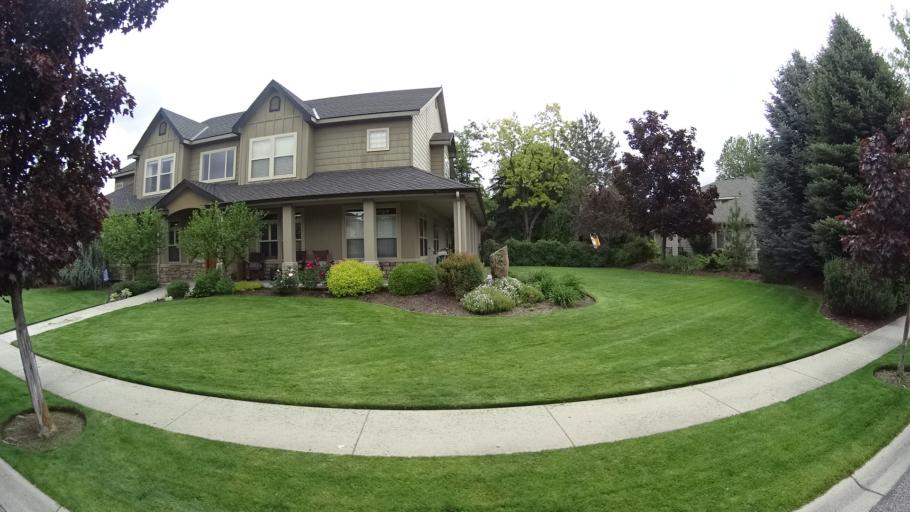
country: US
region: Idaho
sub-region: Ada County
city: Eagle
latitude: 43.6809
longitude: -116.3604
